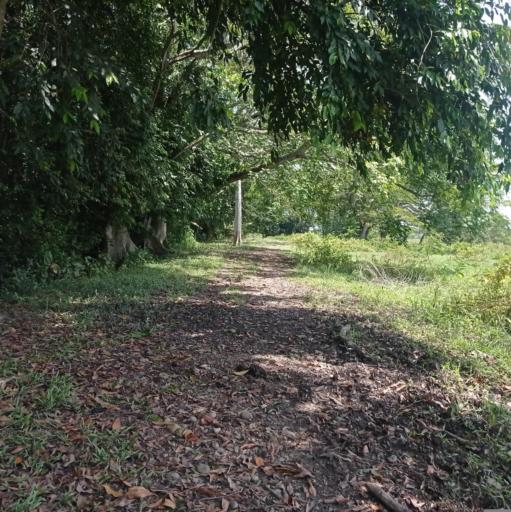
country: CO
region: Santander
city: Barrancabermeja
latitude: 7.0982
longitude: -73.8780
